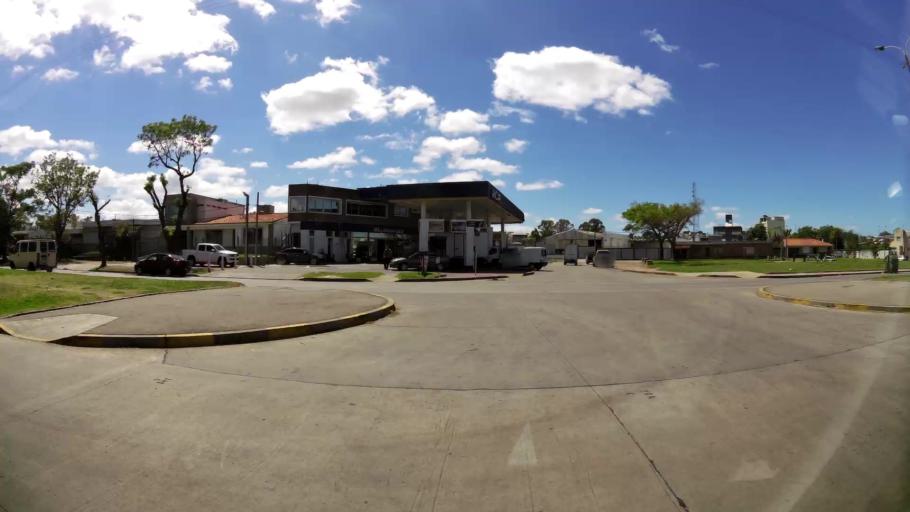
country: UY
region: Montevideo
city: Montevideo
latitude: -34.8588
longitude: -56.1508
